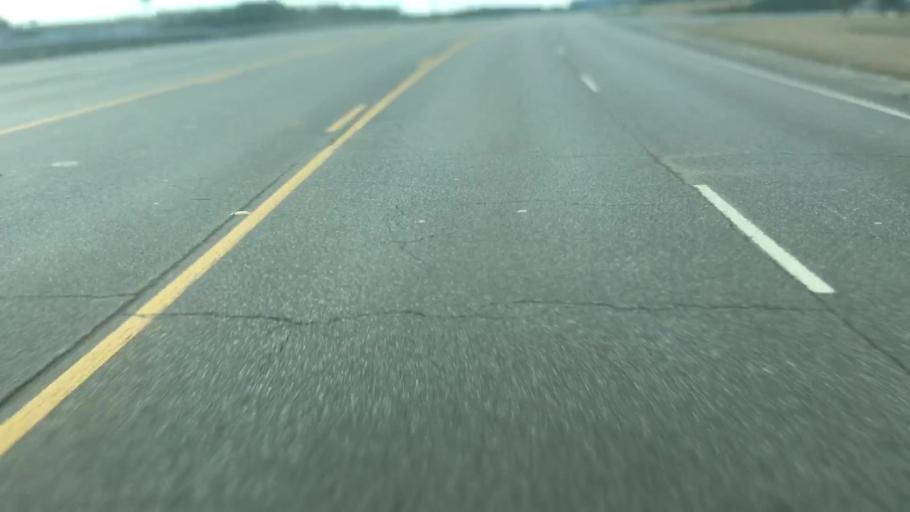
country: US
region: Alabama
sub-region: Walker County
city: Jasper
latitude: 33.8142
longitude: -87.2331
